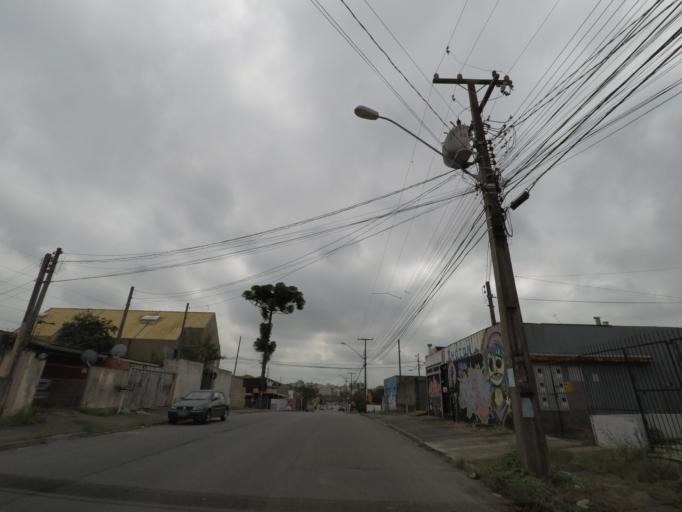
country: BR
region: Parana
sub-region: Curitiba
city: Curitiba
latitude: -25.5159
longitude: -49.3098
